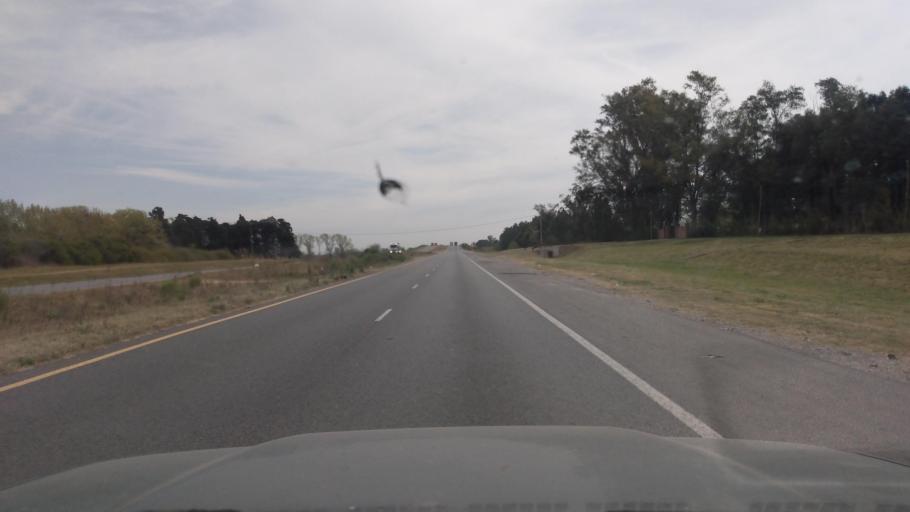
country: AR
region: Buenos Aires
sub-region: Partido de Lujan
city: Lujan
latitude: -34.4866
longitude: -59.0566
